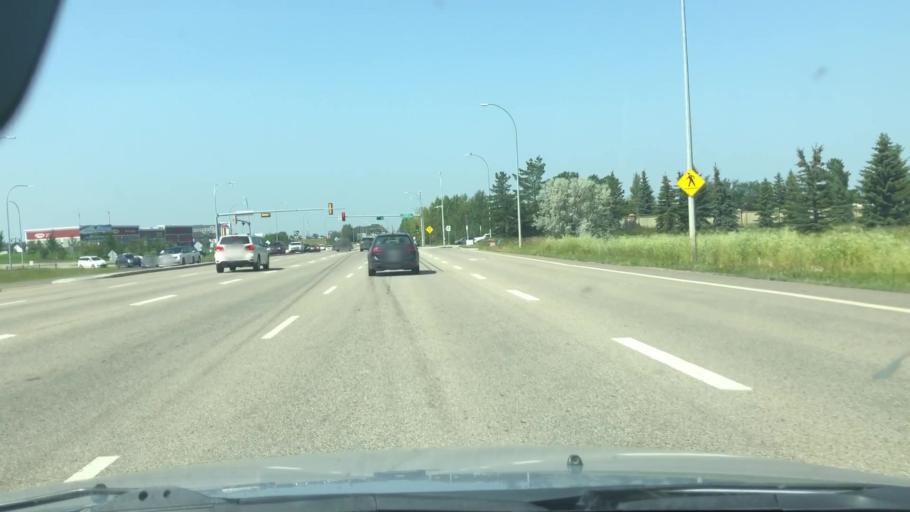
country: CA
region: Alberta
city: St. Albert
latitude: 53.5135
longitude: -113.6795
